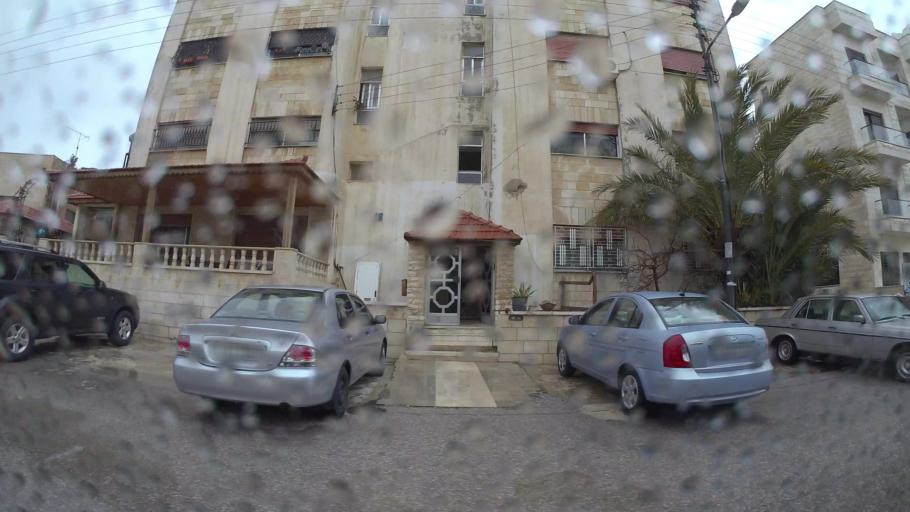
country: JO
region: Amman
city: Wadi as Sir
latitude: 31.9697
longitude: 35.8499
